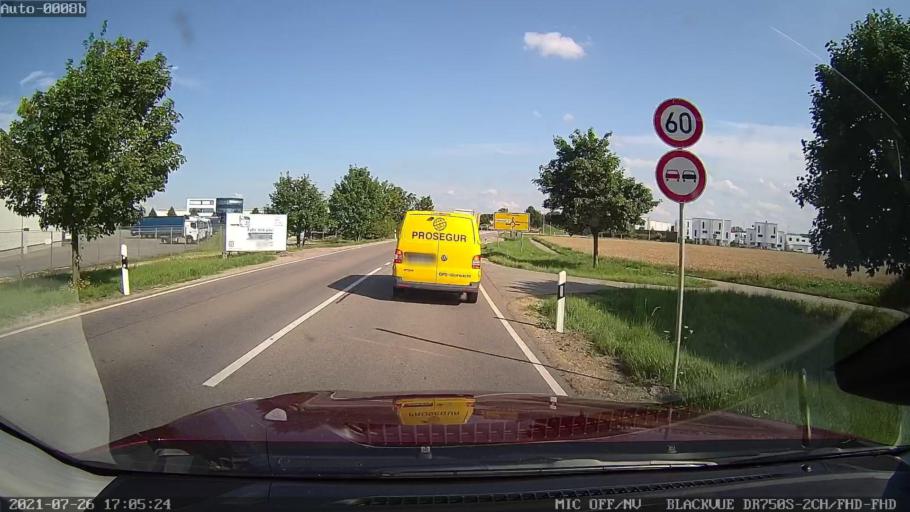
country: DE
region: Bavaria
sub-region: Upper Palatinate
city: Neutraubling
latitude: 48.9931
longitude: 12.2145
